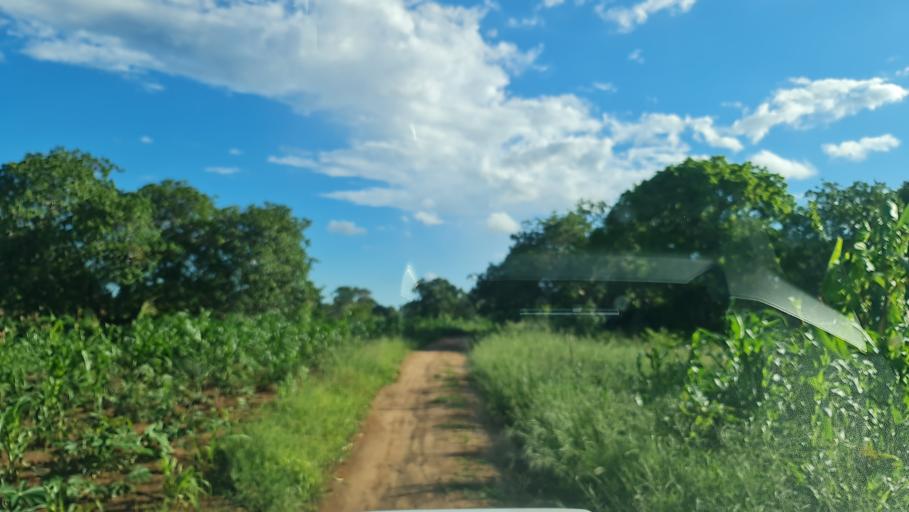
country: MZ
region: Nampula
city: Ilha de Mocambique
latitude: -14.9291
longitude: 40.2204
